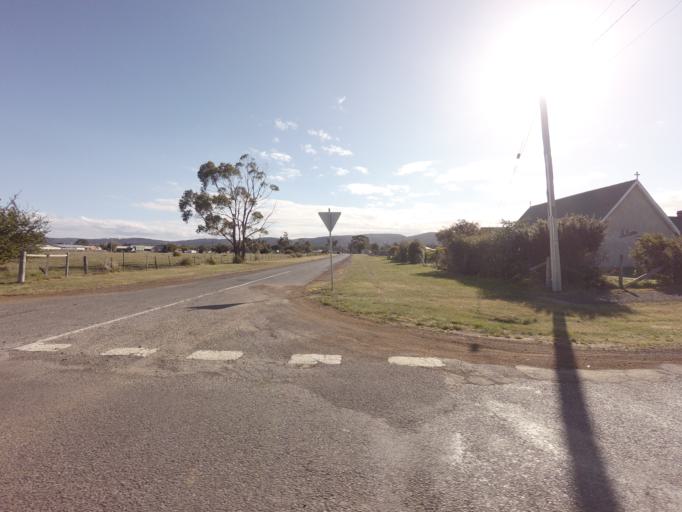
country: AU
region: Tasmania
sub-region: Sorell
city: Sorell
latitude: -42.5037
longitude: 147.9156
